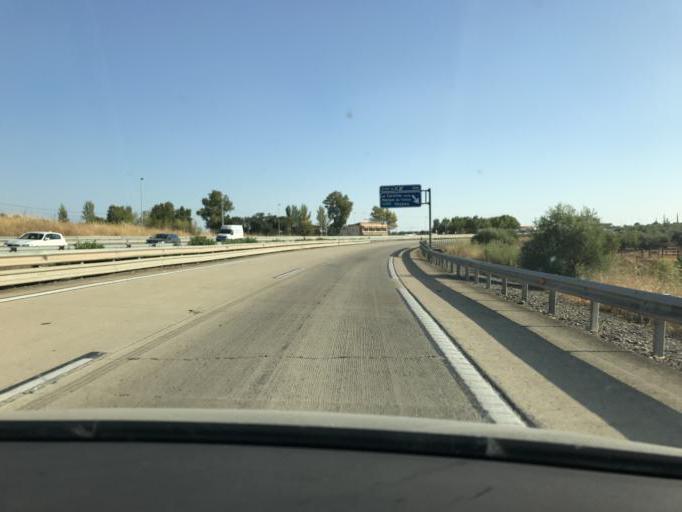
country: ES
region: Andalusia
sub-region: Provincia de Jaen
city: La Carolina
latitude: 38.2858
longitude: -3.5893
